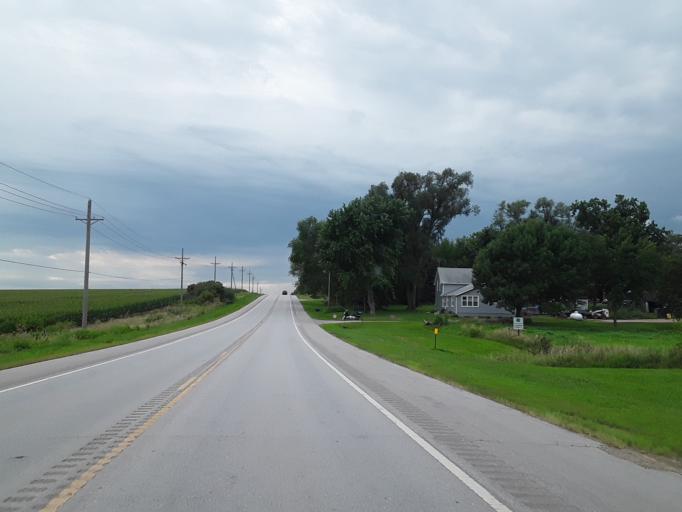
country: US
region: Nebraska
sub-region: Saunders County
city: Yutan
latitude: 41.2338
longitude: -96.3793
